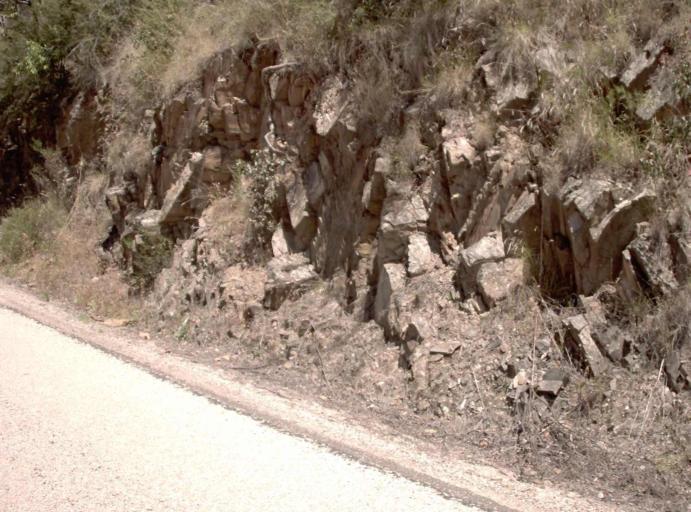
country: AU
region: Victoria
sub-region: East Gippsland
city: Bairnsdale
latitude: -37.4607
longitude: 147.8306
